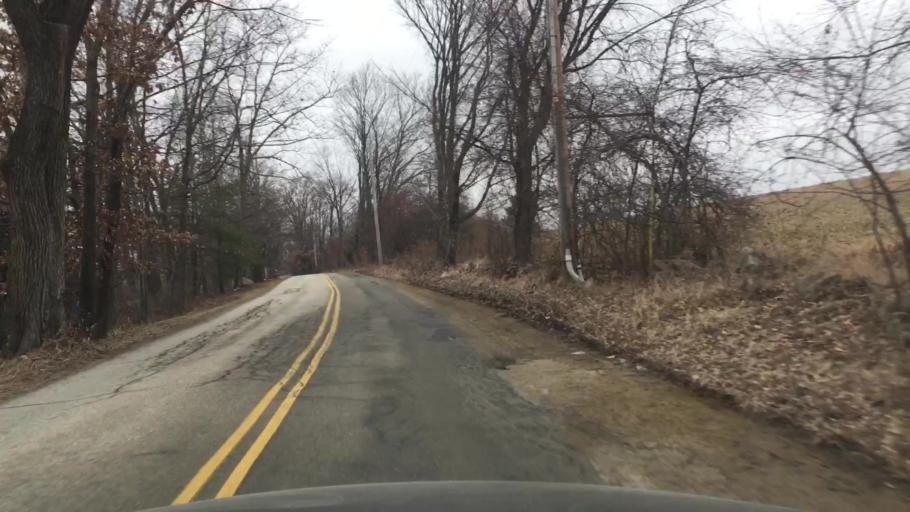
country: US
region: New Hampshire
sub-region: Hillsborough County
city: Mont Vernon
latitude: 42.9328
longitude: -71.6080
